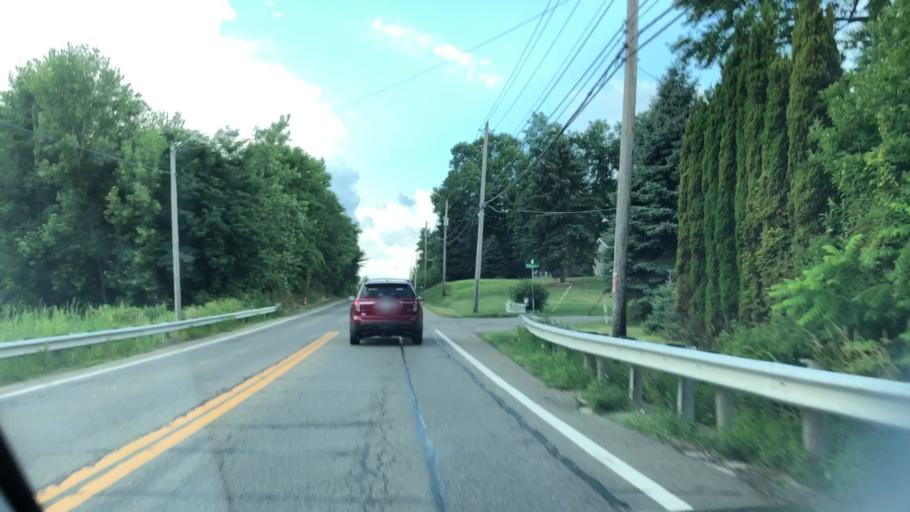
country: US
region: Ohio
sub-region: Summit County
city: Green
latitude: 40.9690
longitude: -81.4936
